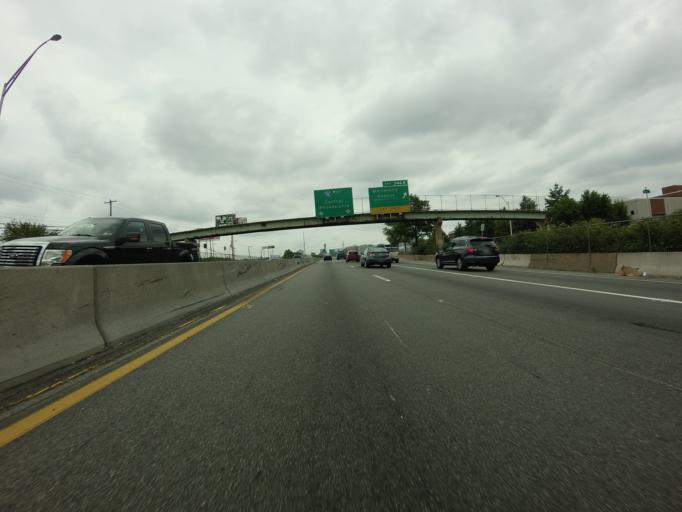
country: US
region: Pennsylvania
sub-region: Philadelphia County
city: Philadelphia
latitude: 39.9330
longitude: -75.2001
